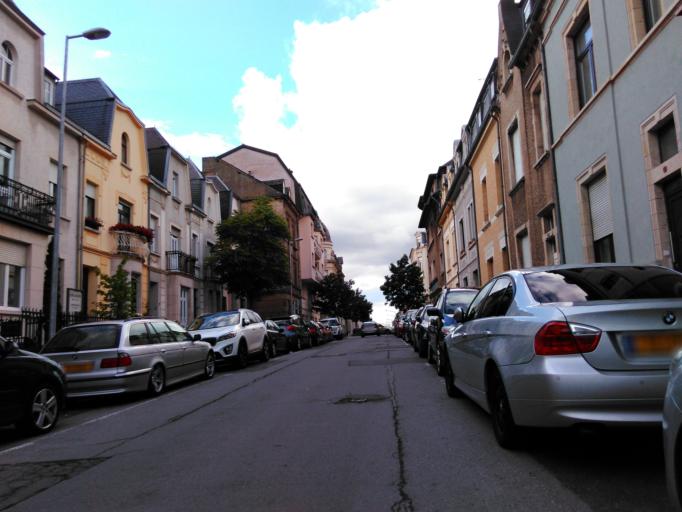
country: LU
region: Luxembourg
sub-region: Canton d'Esch-sur-Alzette
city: Esch-sur-Alzette
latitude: 49.4964
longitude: 5.9792
